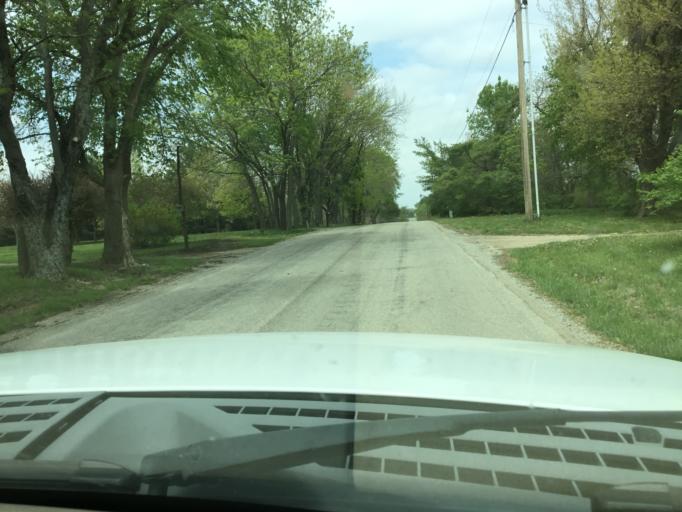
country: US
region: Kansas
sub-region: Shawnee County
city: Topeka
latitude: 38.9805
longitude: -95.5864
